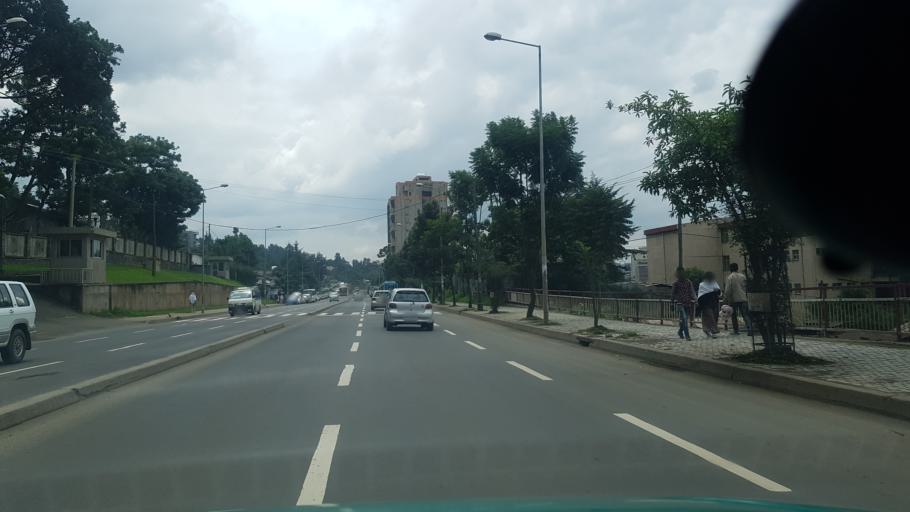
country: ET
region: Adis Abeba
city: Addis Ababa
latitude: 9.0210
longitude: 38.8060
